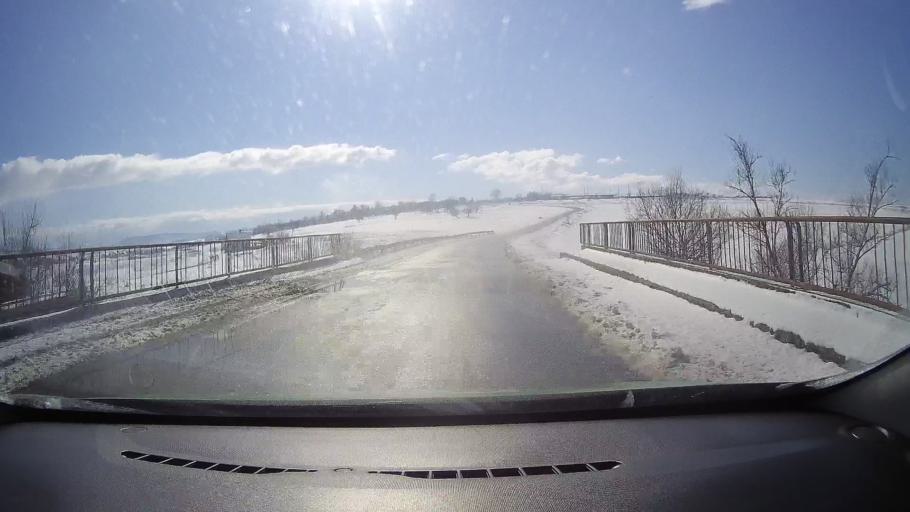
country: RO
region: Sibiu
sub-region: Comuna Rosia
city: Rosia
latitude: 45.8251
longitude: 24.3142
